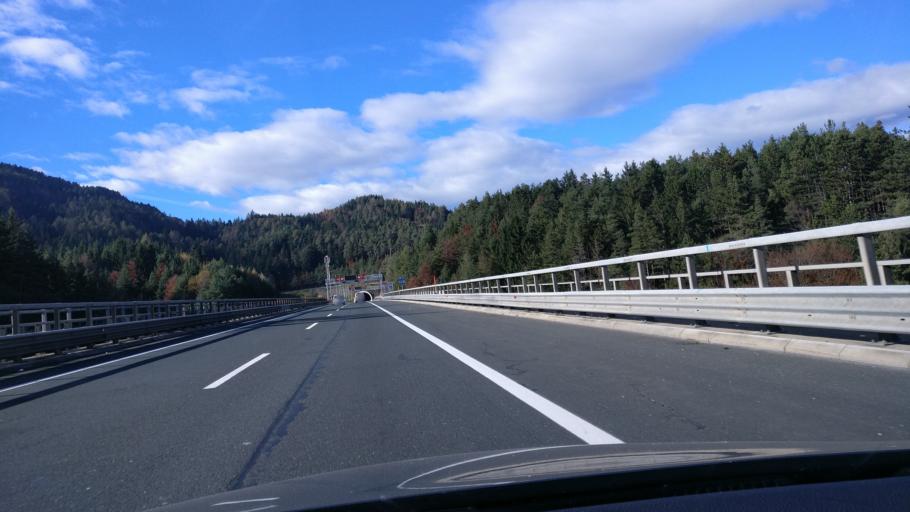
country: AT
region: Carinthia
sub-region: Politischer Bezirk Villach Land
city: Fresach
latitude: 46.6594
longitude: 13.7294
